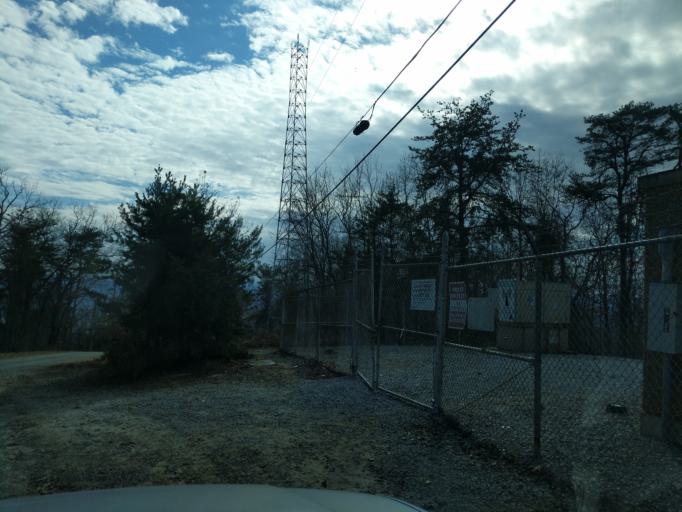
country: US
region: South Carolina
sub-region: Pickens County
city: Pickens
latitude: 34.9000
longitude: -82.6598
